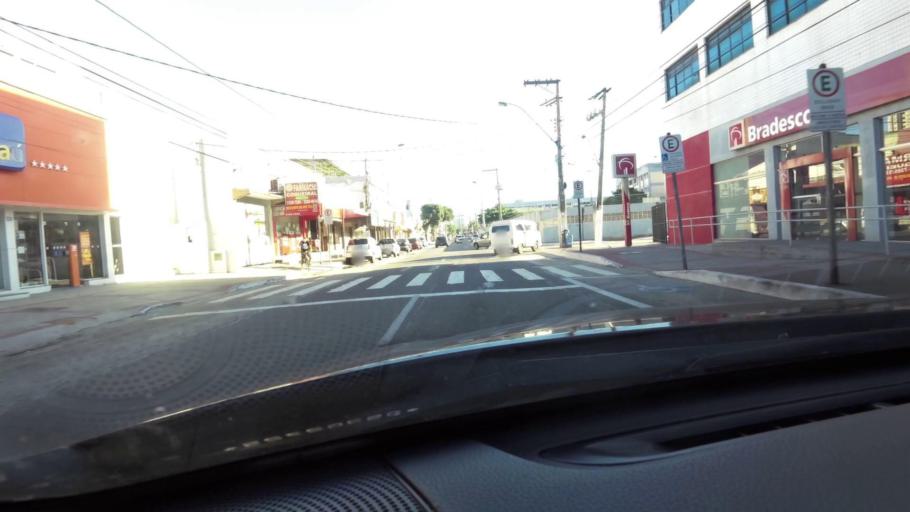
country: BR
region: Espirito Santo
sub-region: Vila Velha
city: Vila Velha
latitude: -20.3601
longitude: -40.2990
